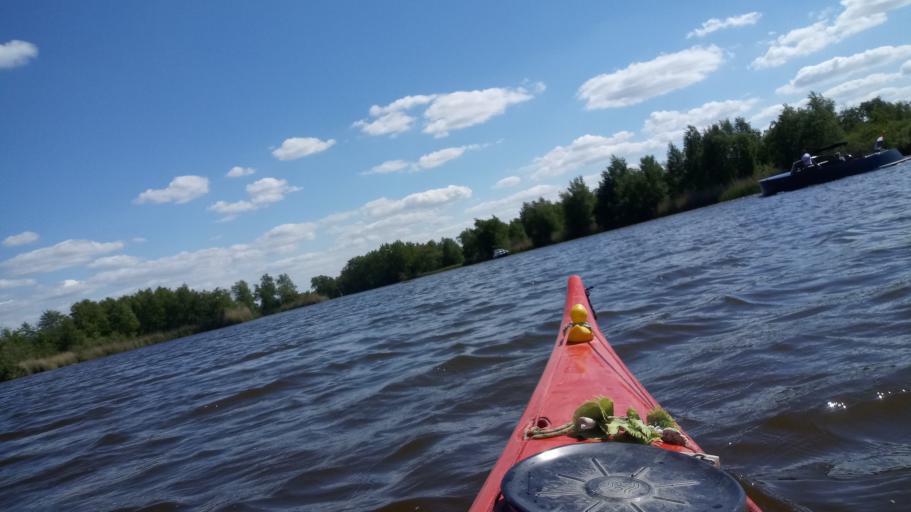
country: NL
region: South Holland
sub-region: Gemeente Nieuwkoop
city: Nieuwkoop
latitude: 52.1426
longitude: 4.7782
